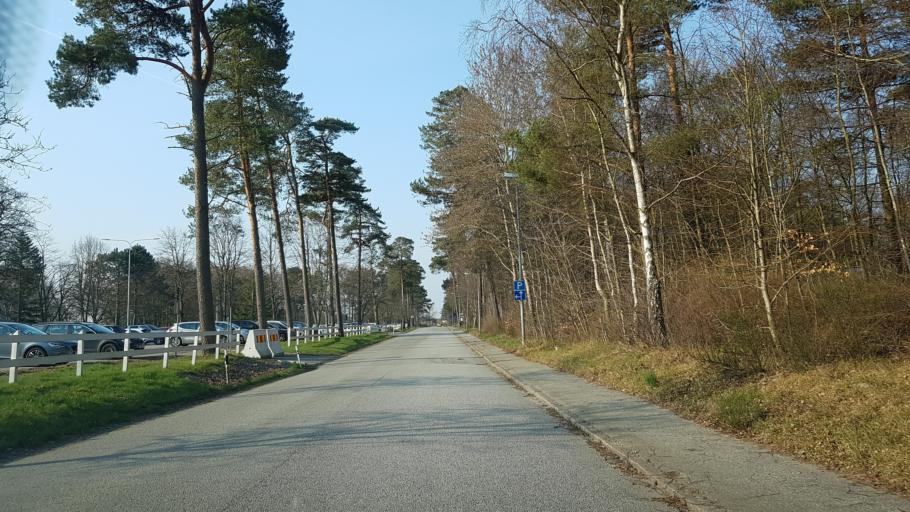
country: SE
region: Skane
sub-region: Ystads Kommun
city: Ystad
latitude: 55.4264
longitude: 13.8489
